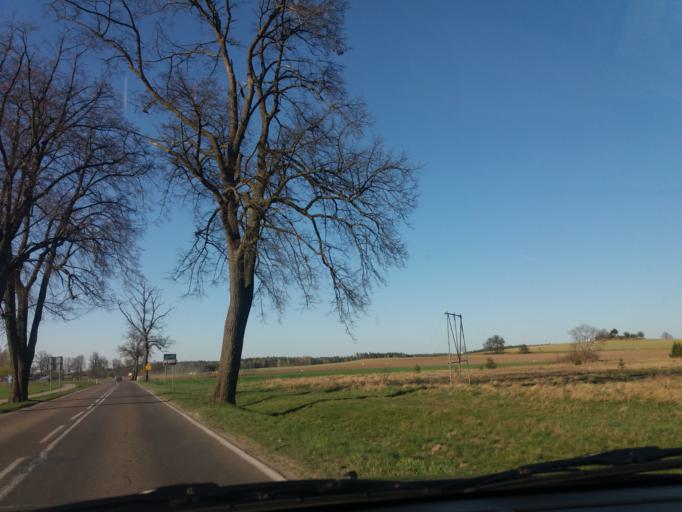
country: PL
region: Warmian-Masurian Voivodeship
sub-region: Powiat nidzicki
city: Nidzica
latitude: 53.3783
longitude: 20.4312
